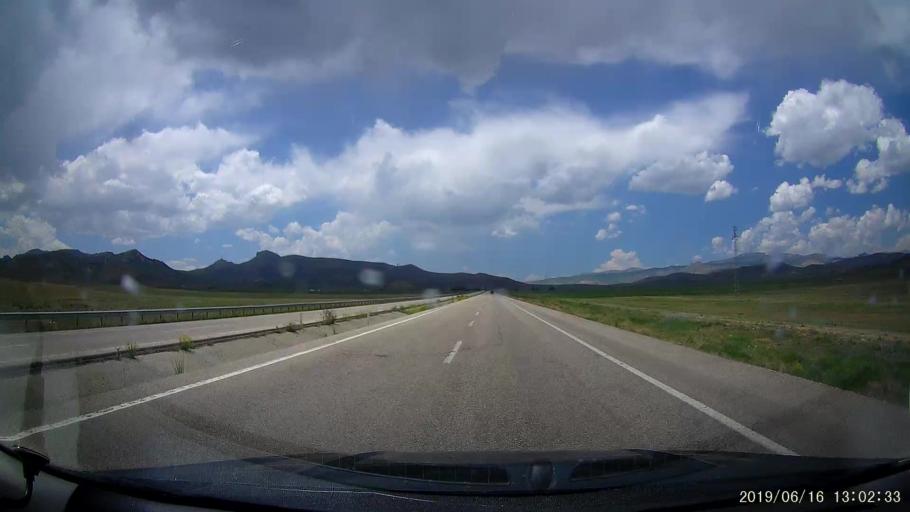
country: TR
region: Agri
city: Sulucem
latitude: 39.5753
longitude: 43.8134
